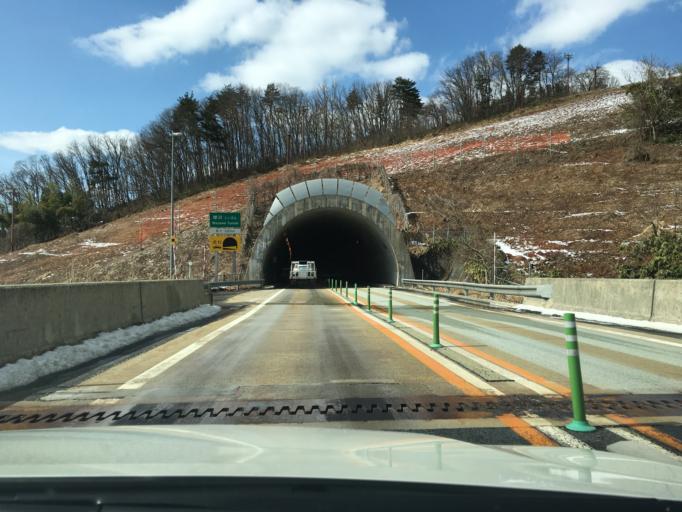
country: JP
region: Yamagata
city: Sagae
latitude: 38.4377
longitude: 140.1286
